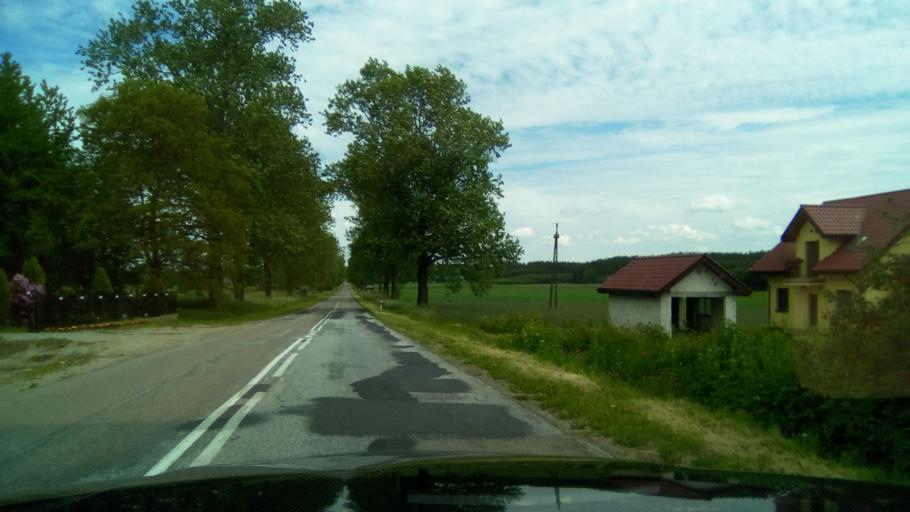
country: PL
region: Pomeranian Voivodeship
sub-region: Powiat bytowski
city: Czarna Dabrowka
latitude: 54.3338
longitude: 17.5304
